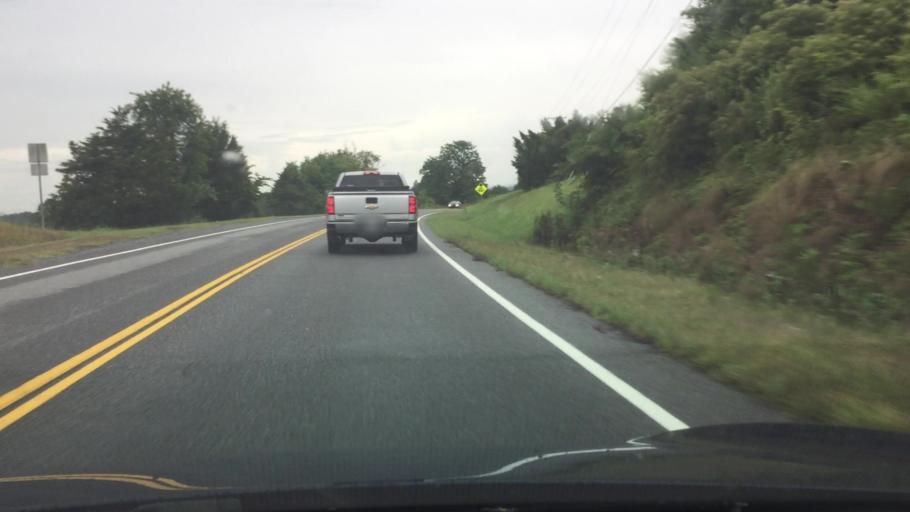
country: US
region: Virginia
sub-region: Bedford County
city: Forest
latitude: 37.3661
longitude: -79.4039
